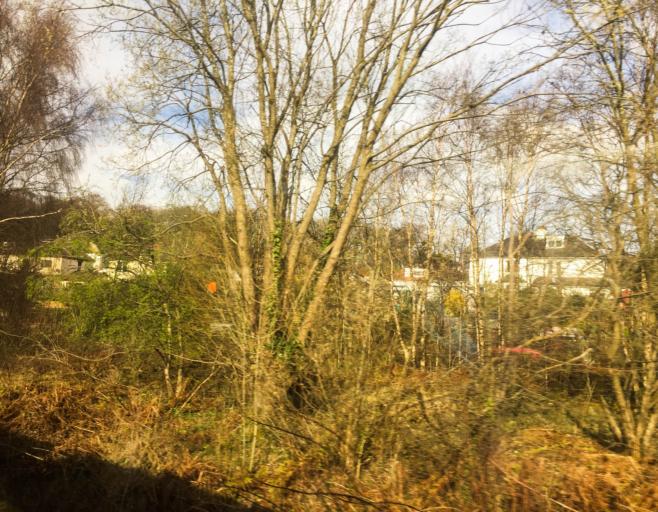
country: GB
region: Scotland
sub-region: East Dunbartonshire
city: Bearsden
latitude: 55.8985
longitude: -4.3226
